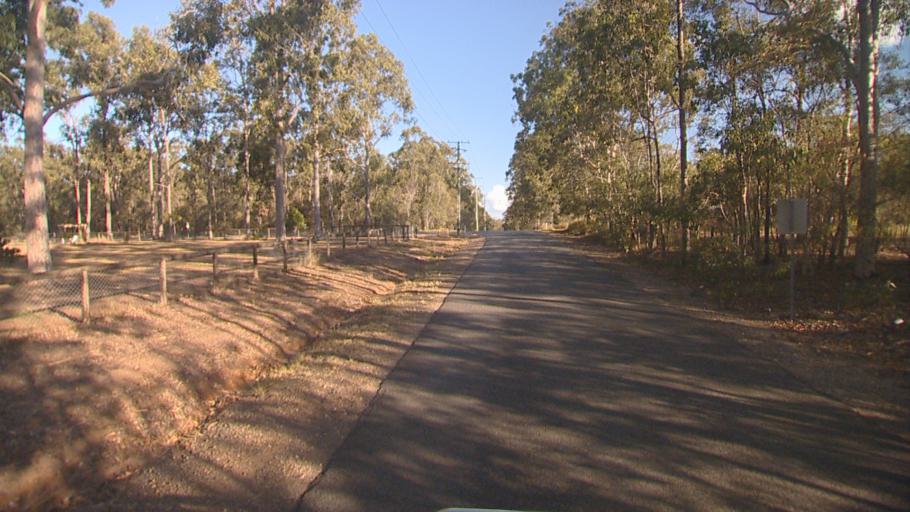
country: AU
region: Queensland
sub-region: Ipswich
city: Springfield Lakes
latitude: -27.7020
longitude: 152.9482
